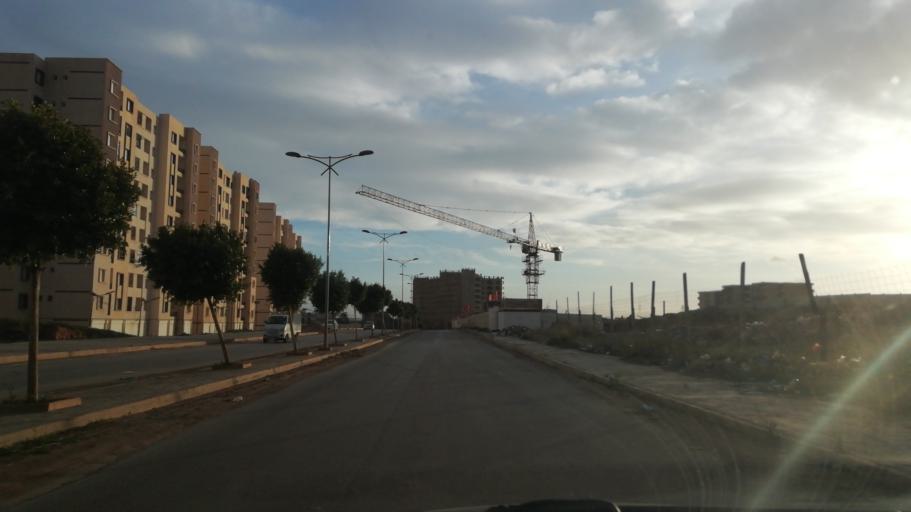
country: DZ
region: Oran
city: Bir el Djir
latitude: 35.6886
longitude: -0.5869
